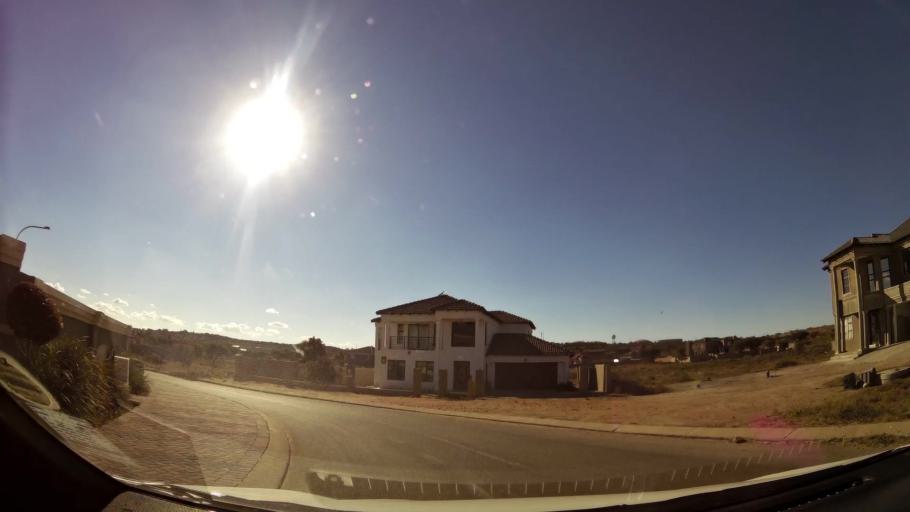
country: ZA
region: Limpopo
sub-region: Capricorn District Municipality
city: Polokwane
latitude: -23.9047
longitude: 29.5054
